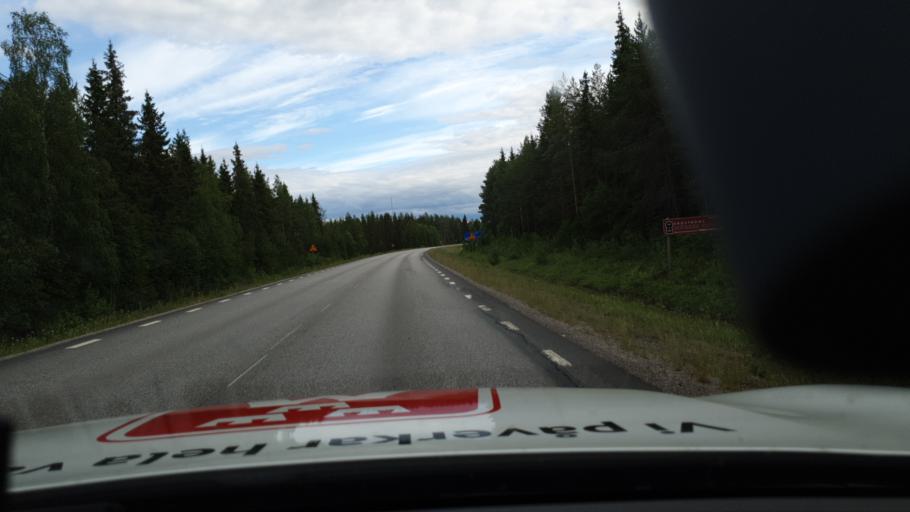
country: SE
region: Norrbotten
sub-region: Overkalix Kommun
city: OEverkalix
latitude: 66.3464
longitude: 22.8287
